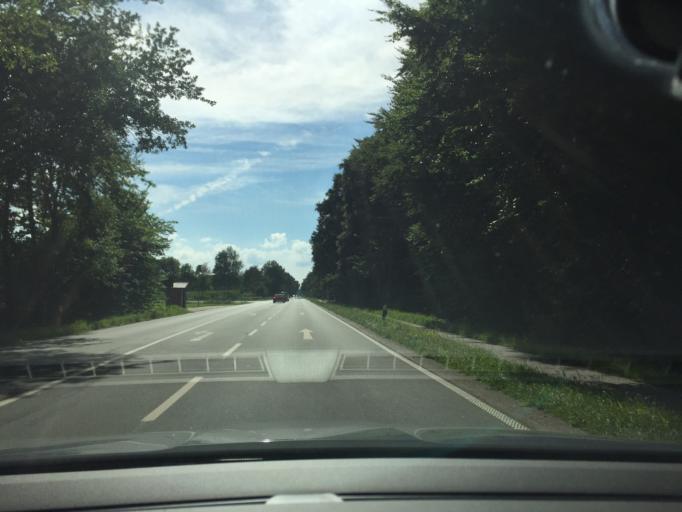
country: DE
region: Lower Saxony
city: Dunum
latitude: 53.5582
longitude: 7.6943
